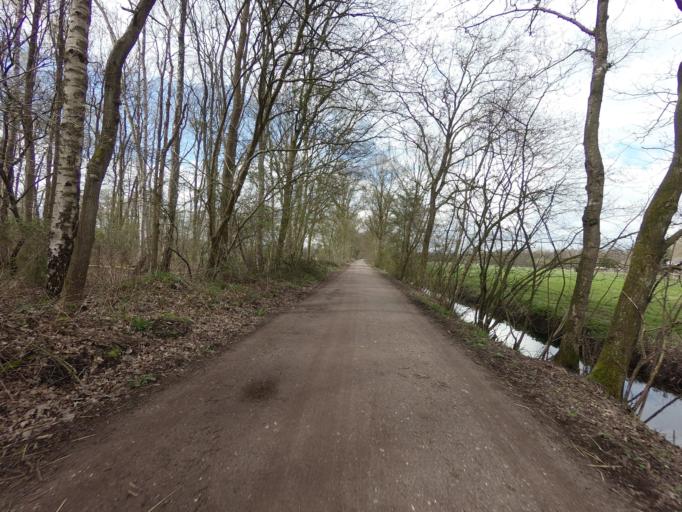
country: NL
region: Utrecht
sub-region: Gemeente Soest
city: Soest
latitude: 52.1642
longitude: 5.2547
